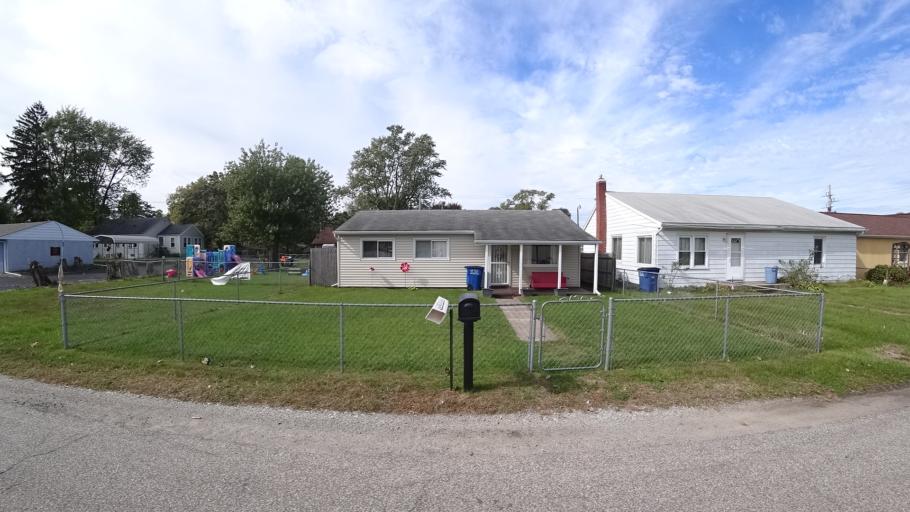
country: US
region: Indiana
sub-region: LaPorte County
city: Trail Creek
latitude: 41.7125
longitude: -86.8685
